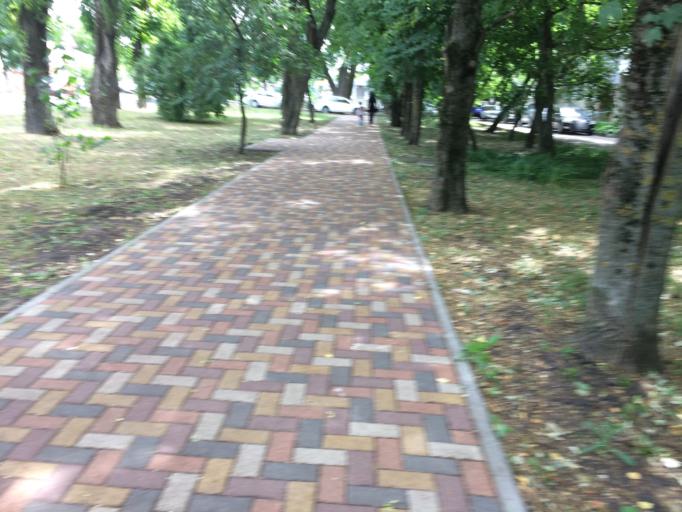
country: RU
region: Stavropol'skiy
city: Stavropol'
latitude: 45.0423
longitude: 41.9535
